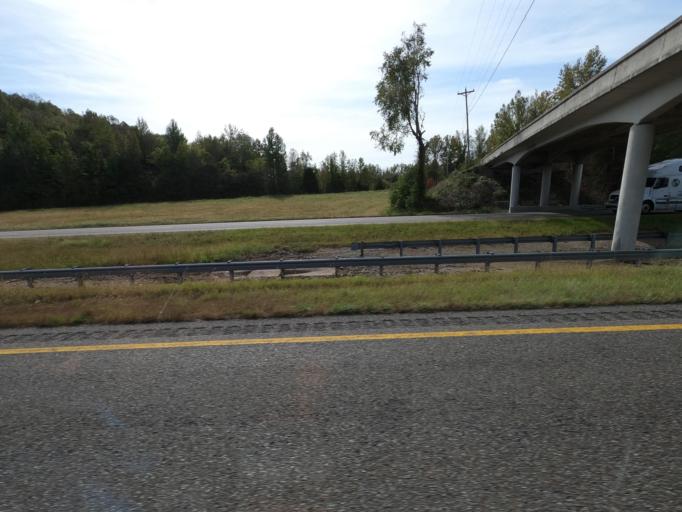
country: US
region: Tennessee
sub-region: Humphreys County
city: New Johnsonville
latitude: 35.8644
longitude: -87.9055
